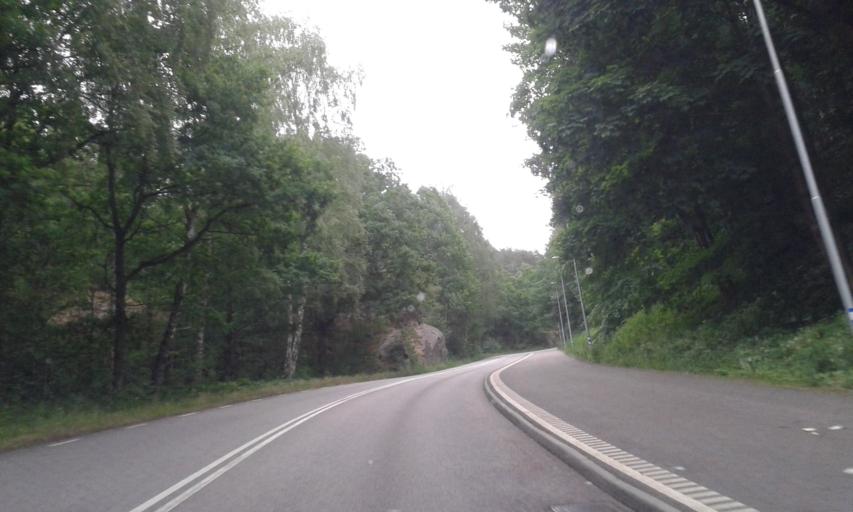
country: SE
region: Vaestra Goetaland
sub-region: Goteborg
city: Eriksbo
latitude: 57.7596
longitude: 12.0204
